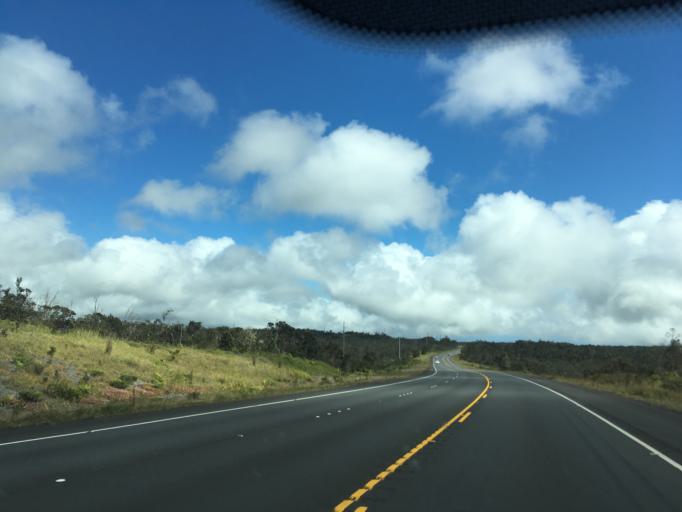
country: US
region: Hawaii
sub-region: Hawaii County
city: Wainaku
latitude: 19.6770
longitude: -155.3184
